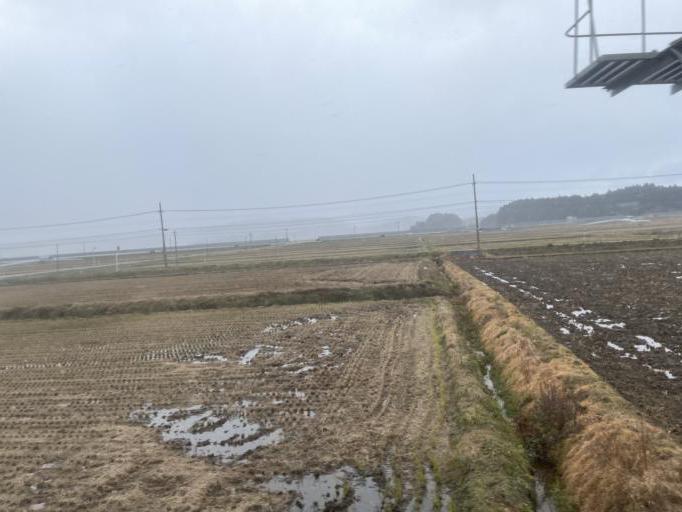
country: JP
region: Aomori
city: Aomori Shi
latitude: 40.9793
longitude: 140.6540
